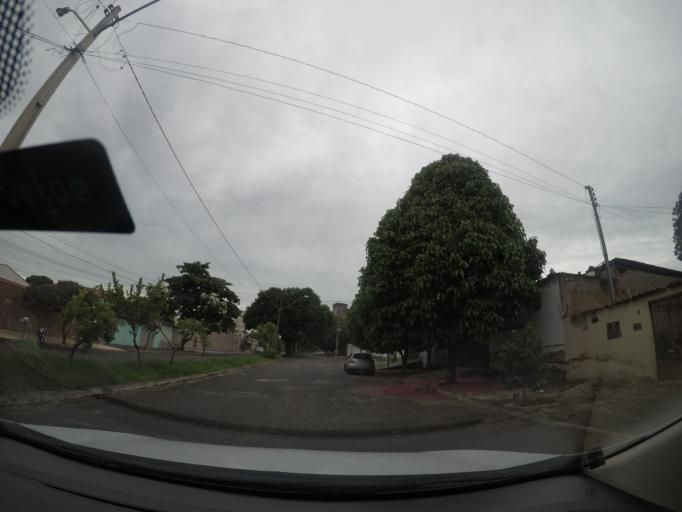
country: BR
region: Goias
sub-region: Goiania
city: Goiania
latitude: -16.6863
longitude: -49.2427
